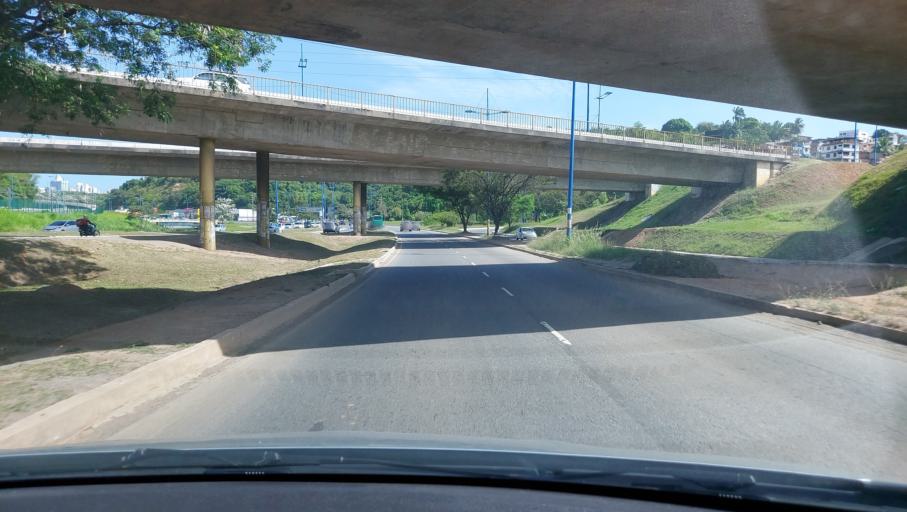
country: BR
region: Bahia
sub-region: Salvador
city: Salvador
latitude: -12.9747
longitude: -38.4772
